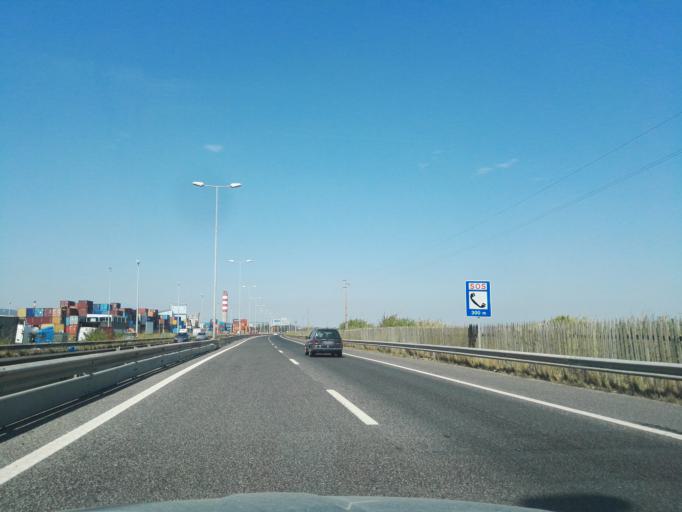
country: PT
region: Lisbon
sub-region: Loures
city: Sao Joao da Talha
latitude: 38.8200
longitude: -9.0860
